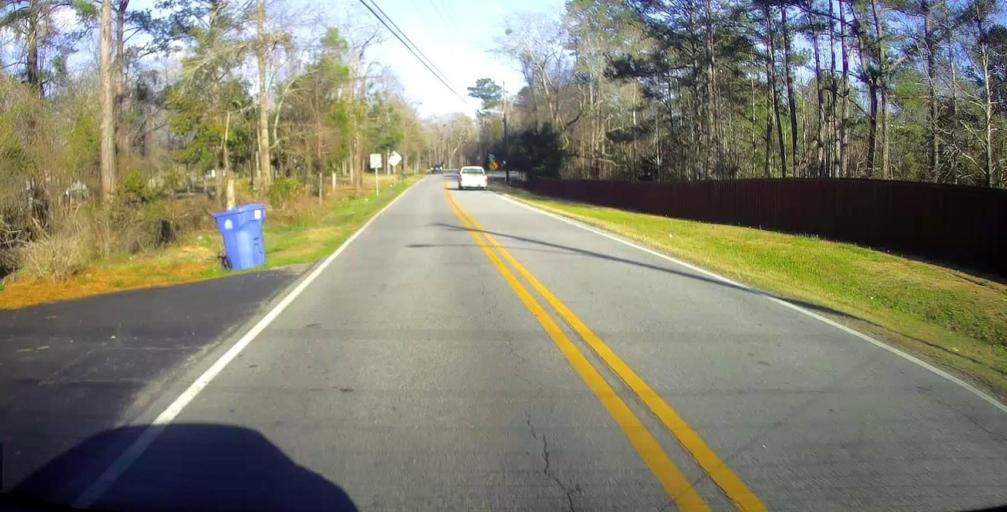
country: US
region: Georgia
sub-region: Harris County
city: Hamilton
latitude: 32.5762
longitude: -84.8138
